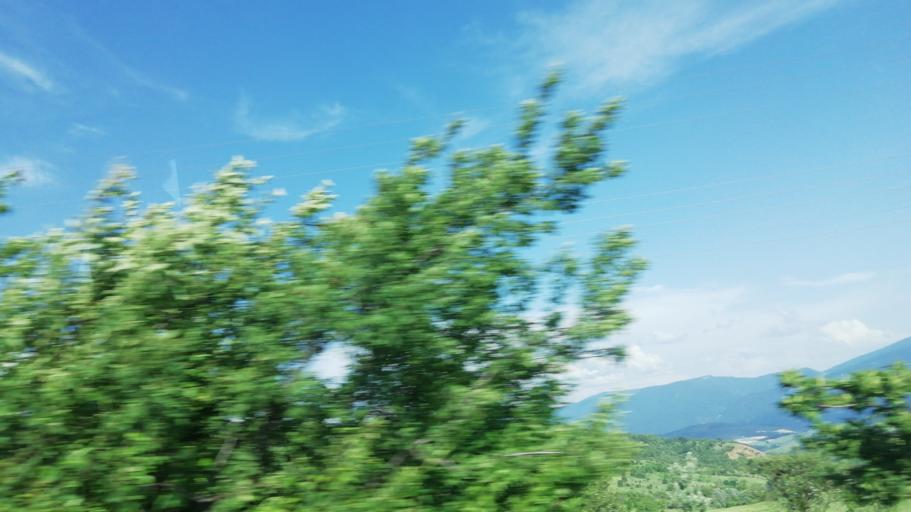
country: TR
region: Karabuk
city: Karabuk
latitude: 41.1030
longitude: 32.5951
